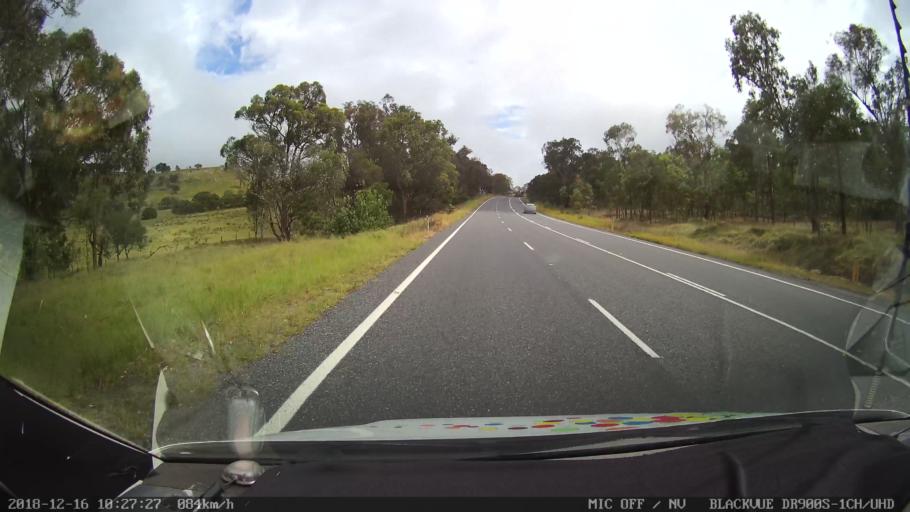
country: AU
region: New South Wales
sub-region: Tenterfield Municipality
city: Carrolls Creek
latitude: -29.1333
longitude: 151.9955
